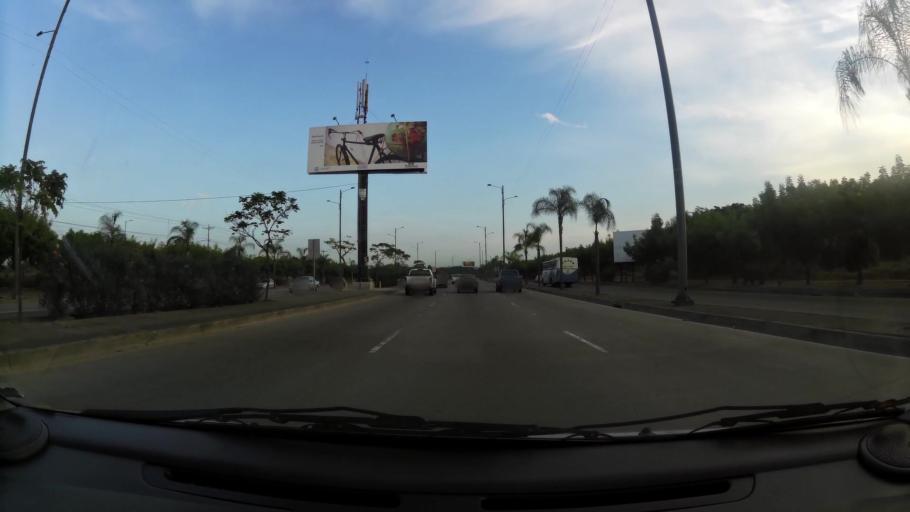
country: EC
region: Guayas
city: Eloy Alfaro
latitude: -2.0985
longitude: -79.8908
